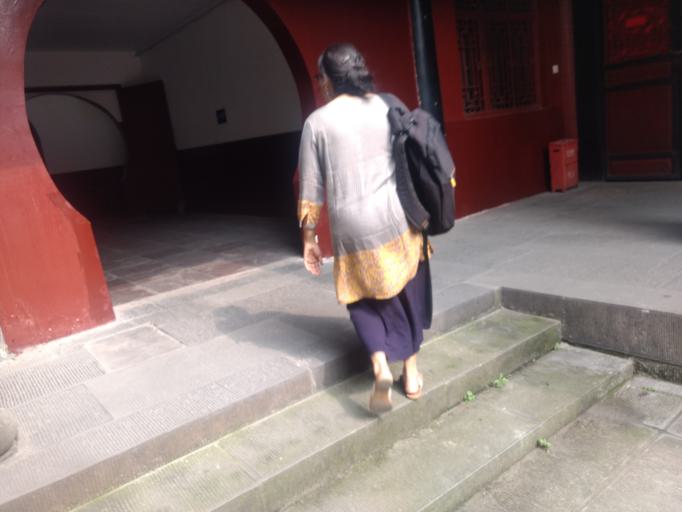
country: CN
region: Sichuan
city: Chengdu
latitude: 30.6774
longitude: 104.0705
